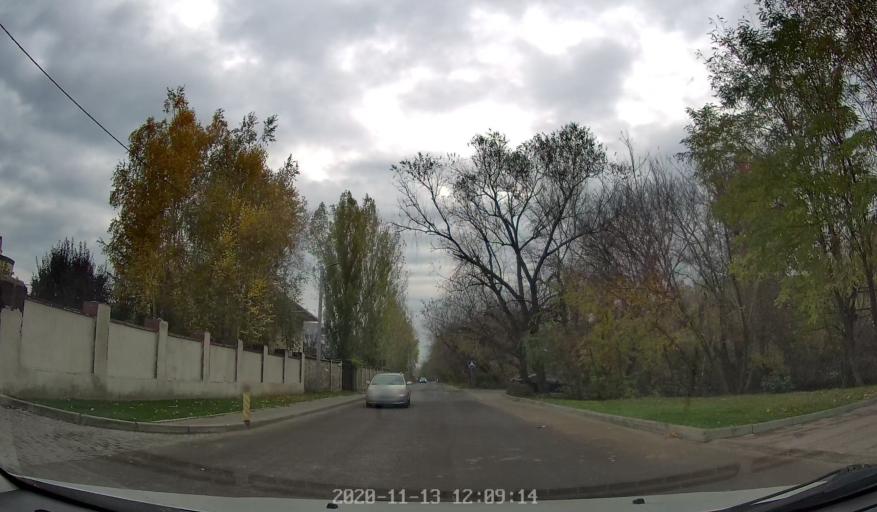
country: MD
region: Chisinau
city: Chisinau
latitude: 46.9600
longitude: 28.8357
